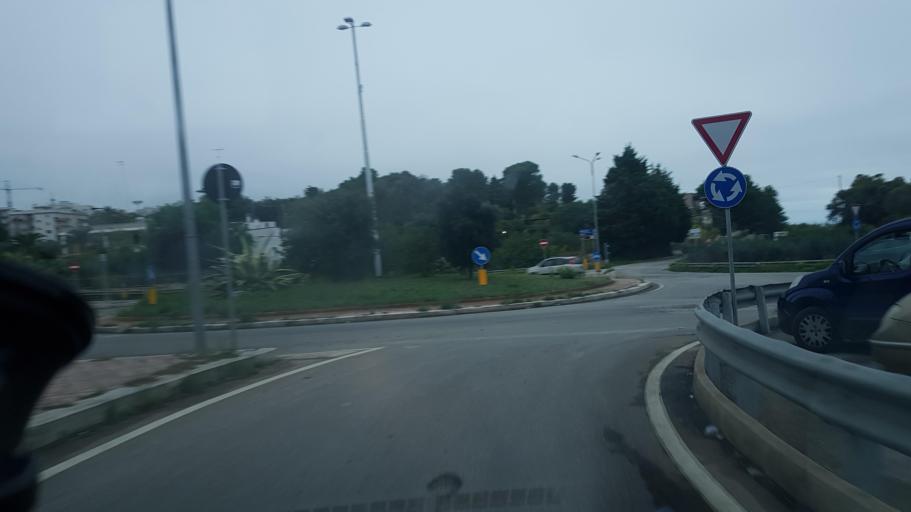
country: IT
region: Apulia
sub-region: Provincia di Brindisi
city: Ostuni
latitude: 40.7241
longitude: 17.5922
